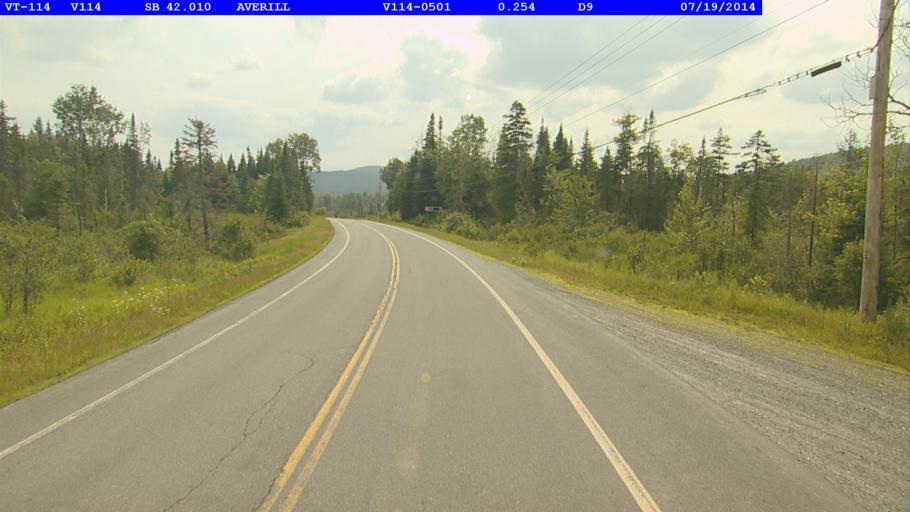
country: CA
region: Quebec
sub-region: Estrie
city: Coaticook
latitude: 45.0023
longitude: -71.7051
